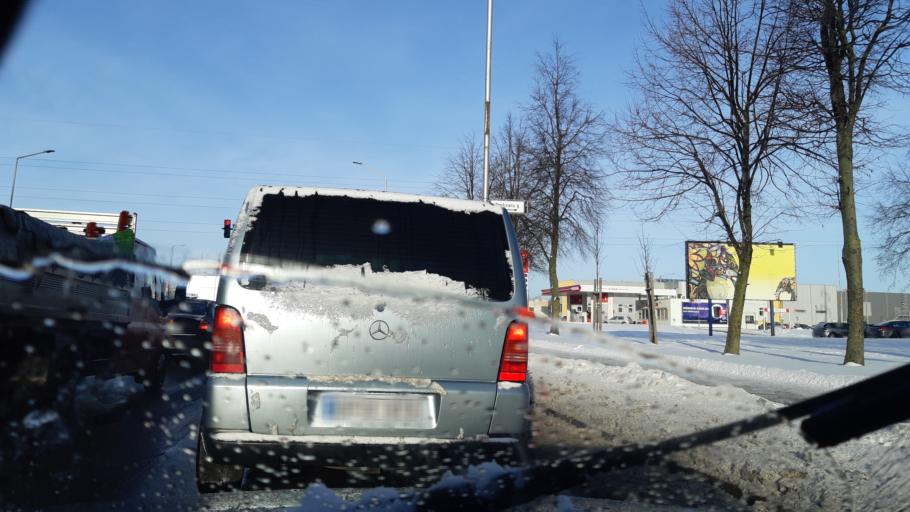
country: LT
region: Kauno apskritis
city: Dainava (Kaunas)
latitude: 54.9261
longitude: 23.9753
